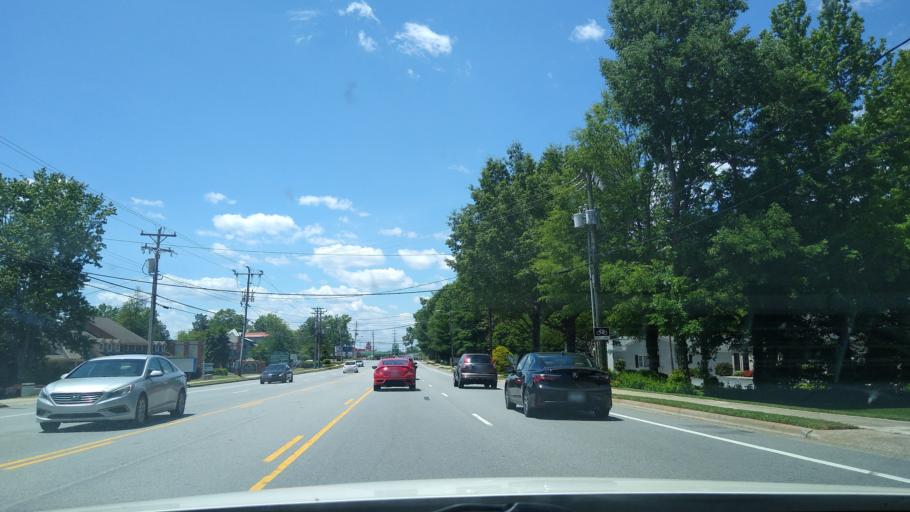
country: US
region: North Carolina
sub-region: Guilford County
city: Greensboro
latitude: 36.0892
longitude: -79.8808
